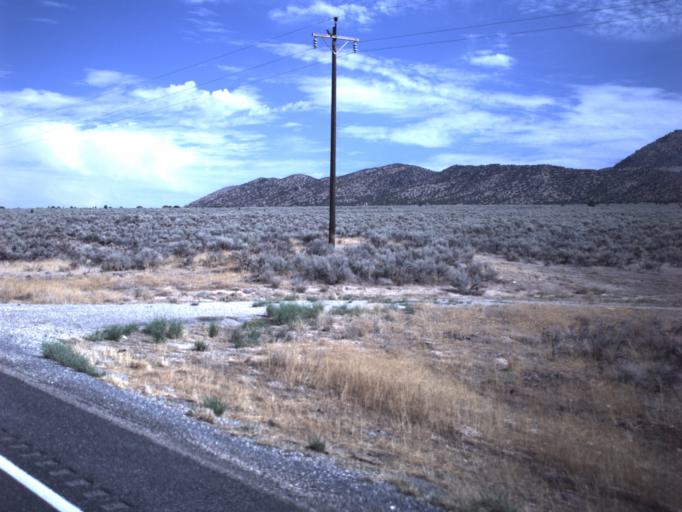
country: US
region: Utah
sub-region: Sanpete County
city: Gunnison
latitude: 39.2747
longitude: -111.8751
